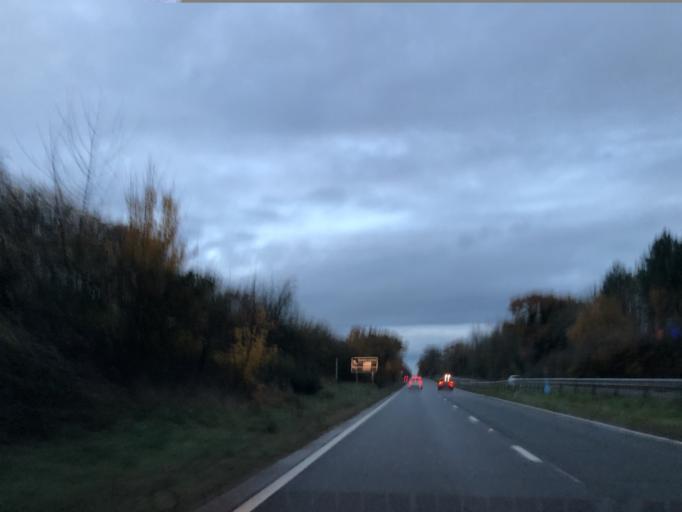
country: GB
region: England
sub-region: Solihull
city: Bickenhill
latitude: 52.4597
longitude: -1.7027
